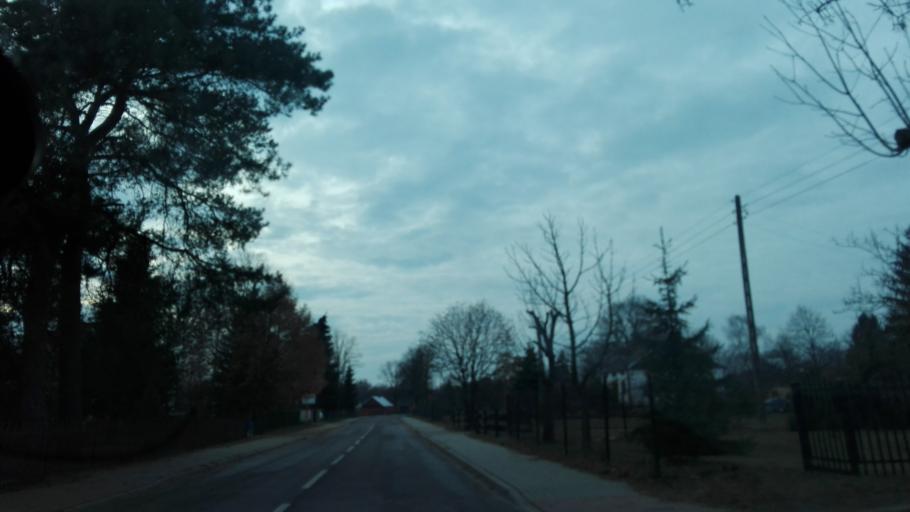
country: PL
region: Lublin Voivodeship
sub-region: Powiat bialski
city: Slawatycze
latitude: 51.7170
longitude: 23.4938
